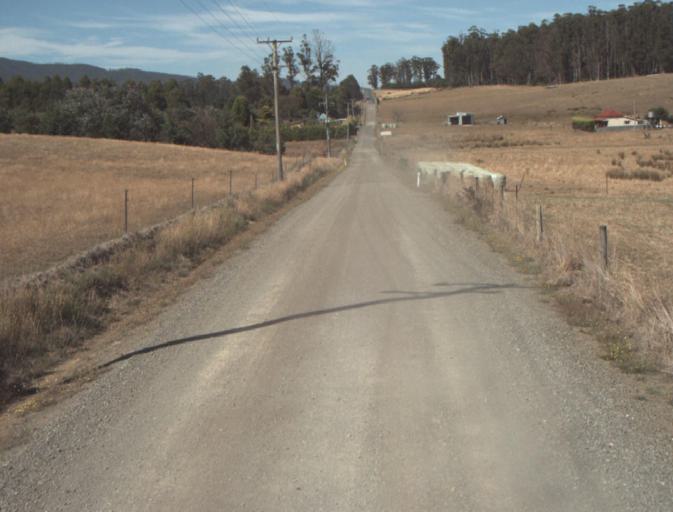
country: AU
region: Tasmania
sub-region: Launceston
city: Mayfield
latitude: -41.2245
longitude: 147.2370
